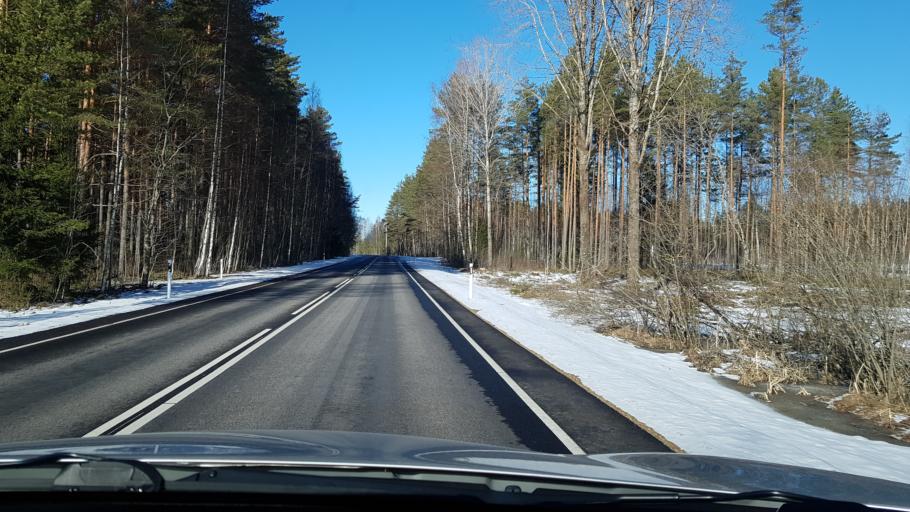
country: EE
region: Polvamaa
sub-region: Raepina vald
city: Rapina
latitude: 57.9889
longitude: 27.5638
